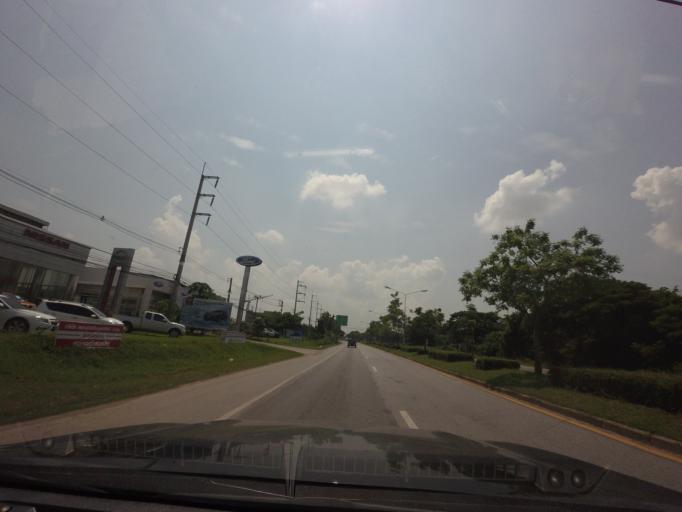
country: TH
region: Uttaradit
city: Uttaradit
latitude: 17.6111
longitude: 100.1233
